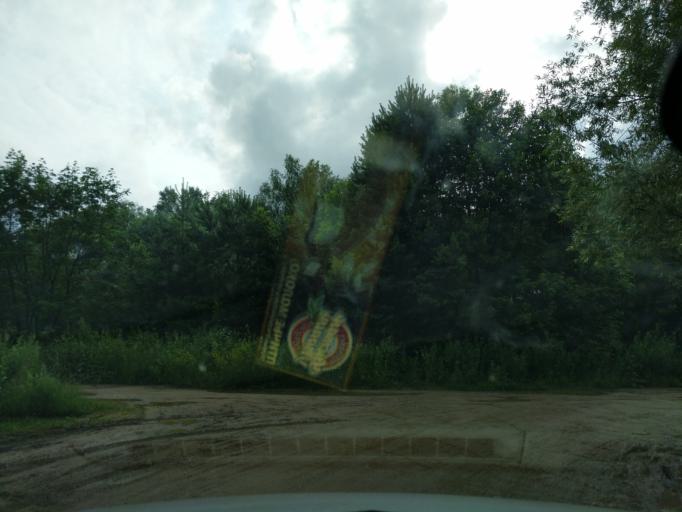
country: RU
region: Kaluga
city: Nikola-Lenivets
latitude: 54.7609
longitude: 35.5990
